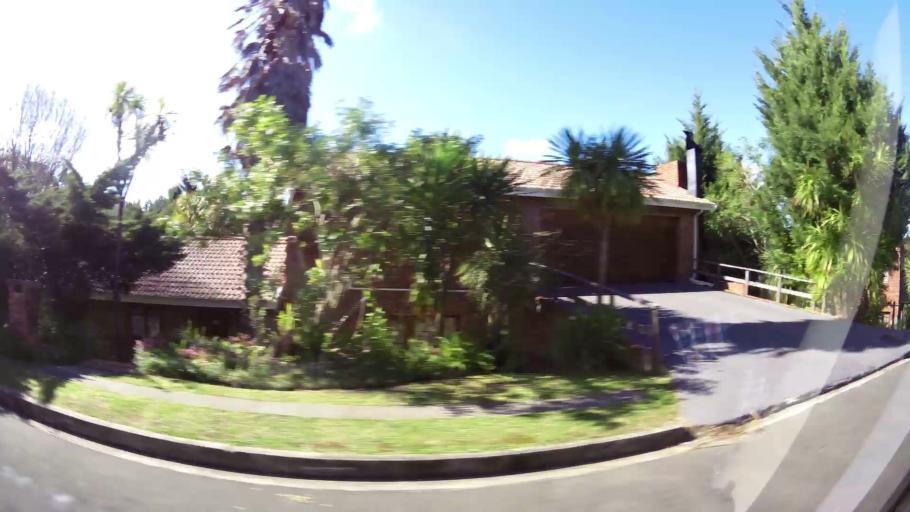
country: ZA
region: Western Cape
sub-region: Eden District Municipality
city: George
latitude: -33.9469
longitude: 22.4809
